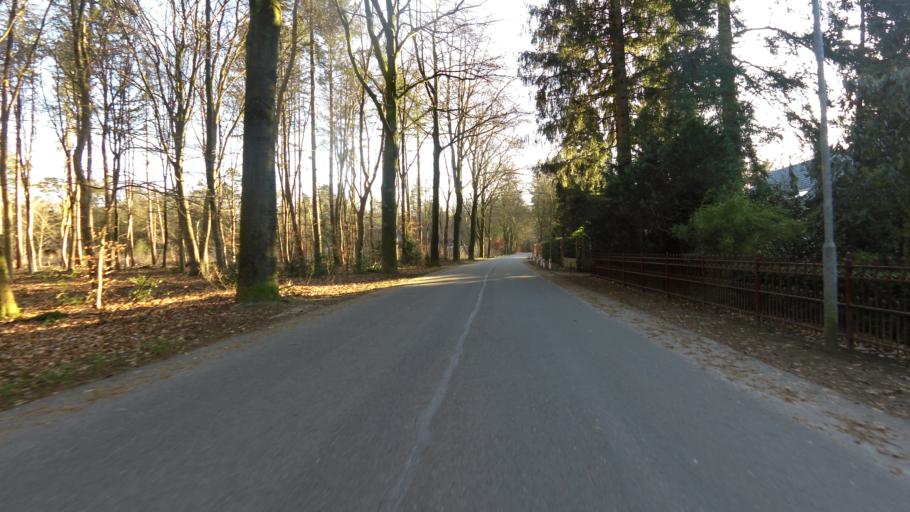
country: NL
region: Gelderland
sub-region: Gemeente Putten
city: Putten
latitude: 52.2592
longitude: 5.6268
